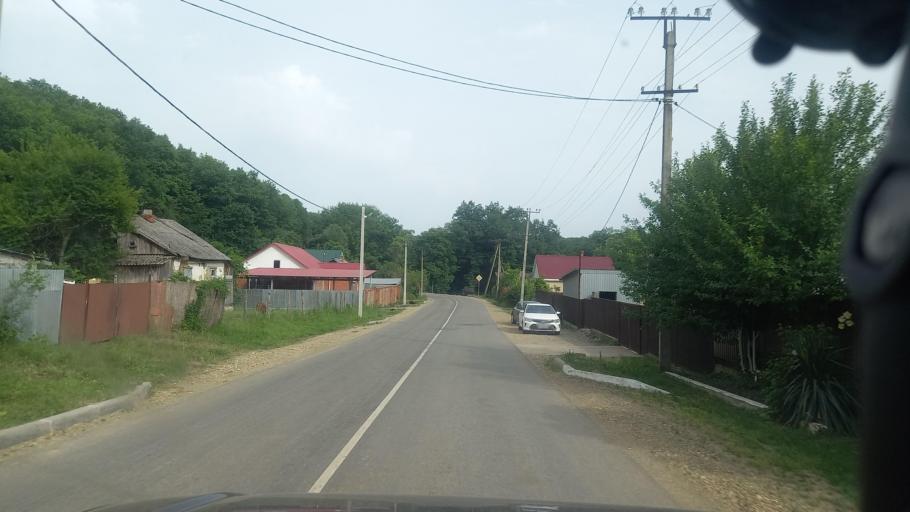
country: RU
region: Krasnodarskiy
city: Goryachiy Klyuch
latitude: 44.6051
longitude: 39.0013
